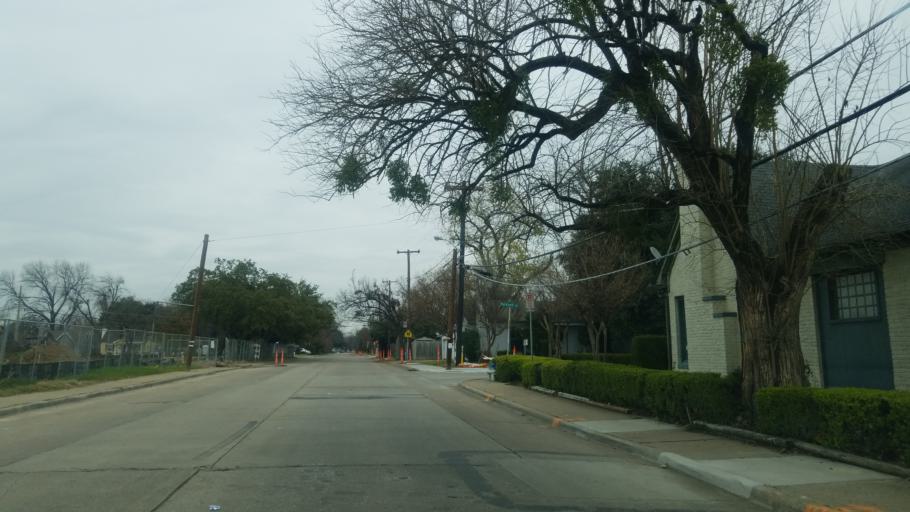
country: US
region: Texas
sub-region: Dallas County
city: Highland Park
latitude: 32.8196
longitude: -96.8314
